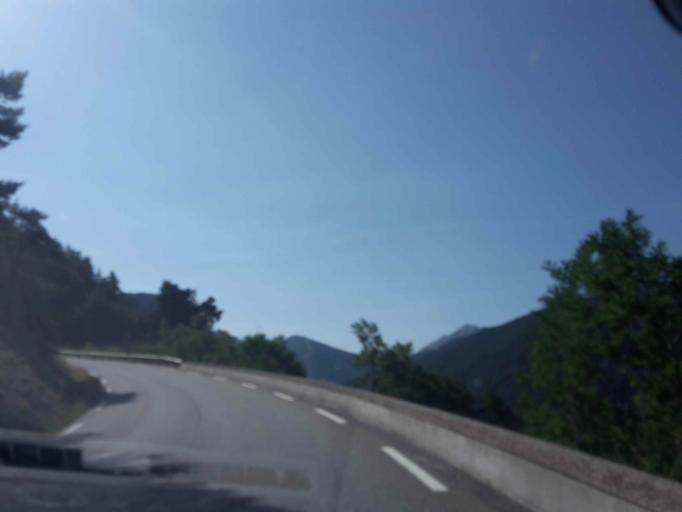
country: FR
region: Provence-Alpes-Cote d'Azur
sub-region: Departement des Hautes-Alpes
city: Guillestre
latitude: 44.6320
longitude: 6.6766
